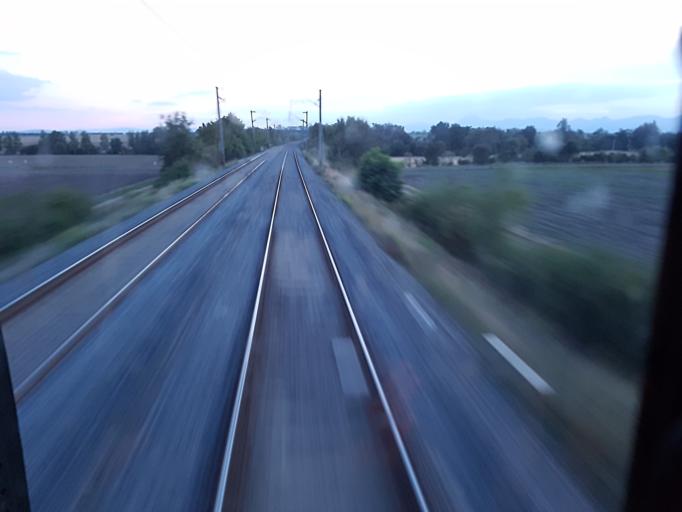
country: FR
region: Auvergne
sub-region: Departement du Puy-de-Dome
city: Ennezat
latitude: 45.9300
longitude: 3.2325
